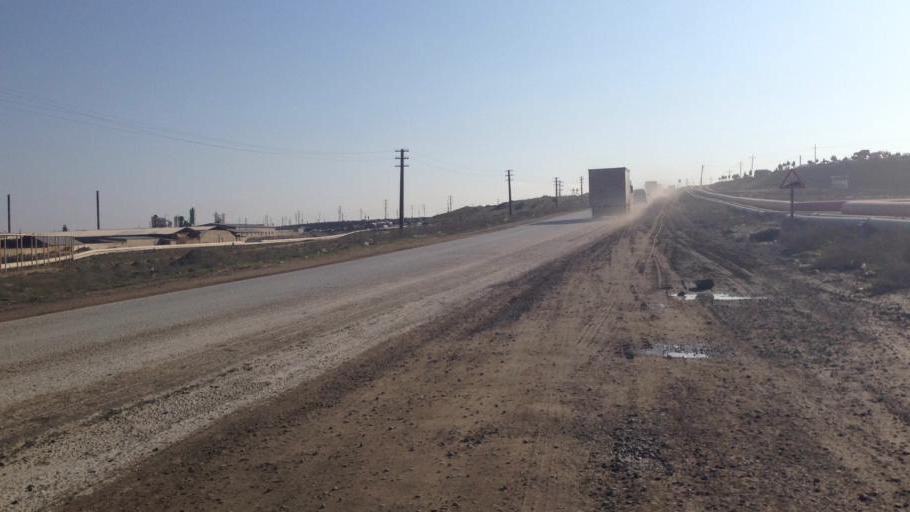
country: AZ
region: Abseron
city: Digah
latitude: 40.4659
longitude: 49.8873
